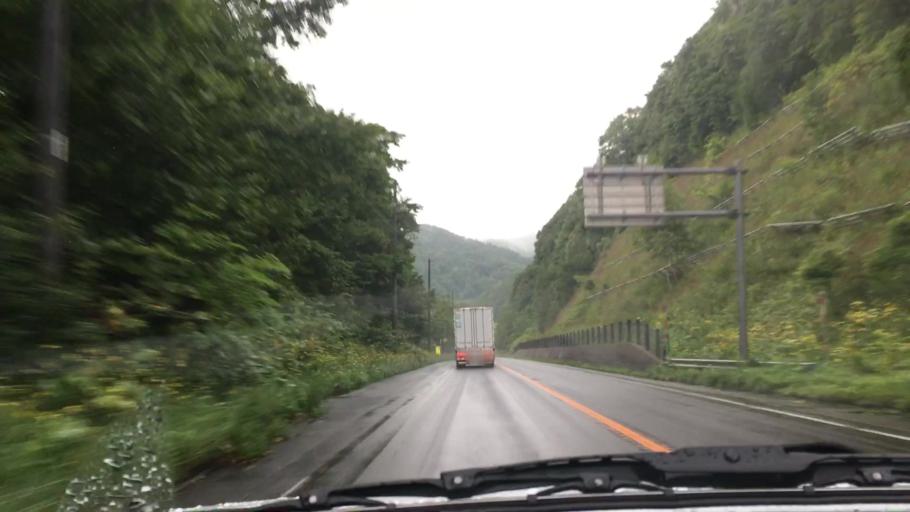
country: JP
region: Hokkaido
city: Niseko Town
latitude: 42.5967
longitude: 140.5886
